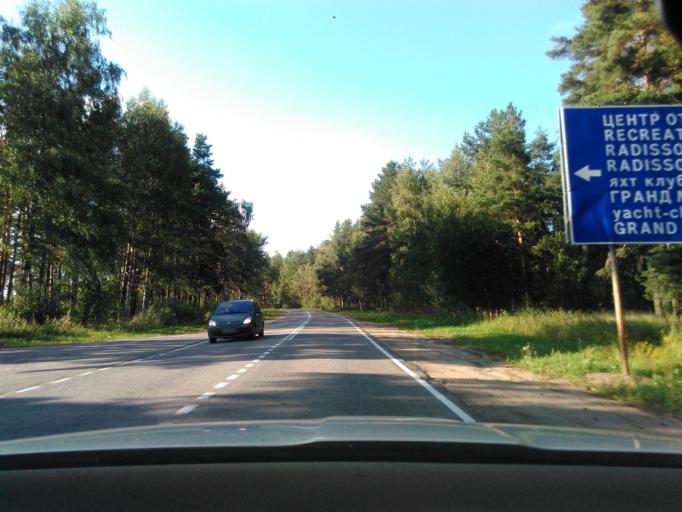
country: RU
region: Tverskaya
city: Zavidovo
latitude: 56.5910
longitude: 36.5416
